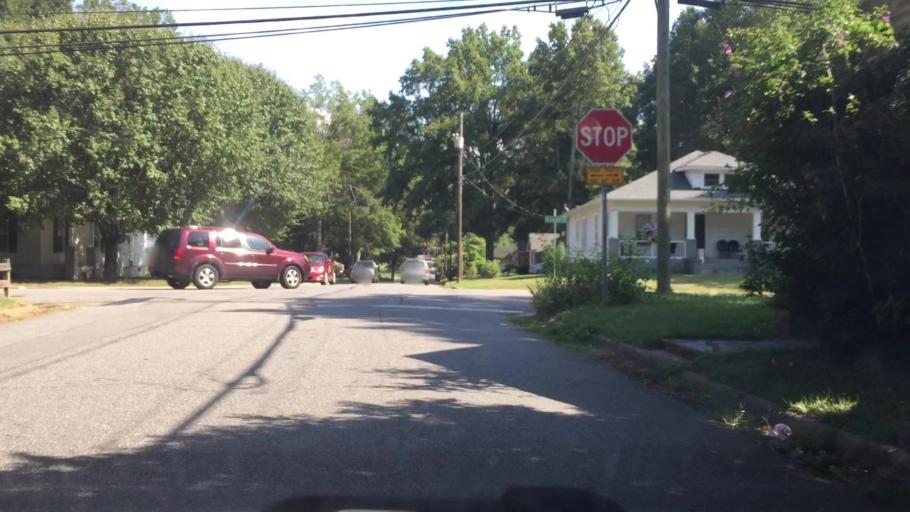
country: US
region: North Carolina
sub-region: Iredell County
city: Mooresville
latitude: 35.5859
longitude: -80.8003
